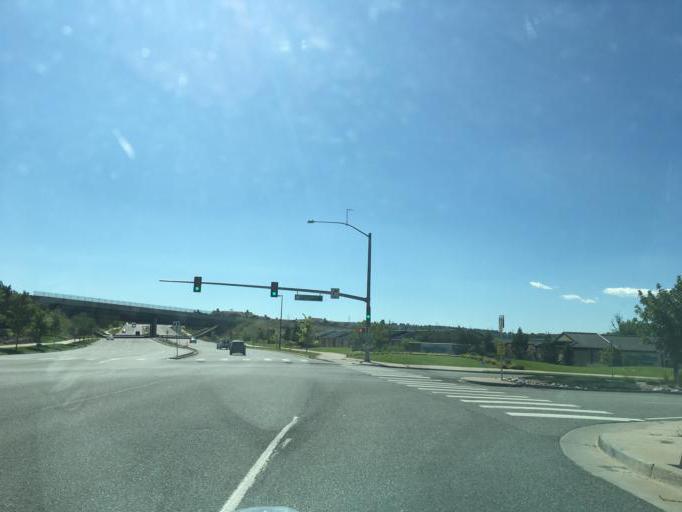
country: US
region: Colorado
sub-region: Douglas County
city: Parker
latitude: 39.5912
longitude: -104.7212
